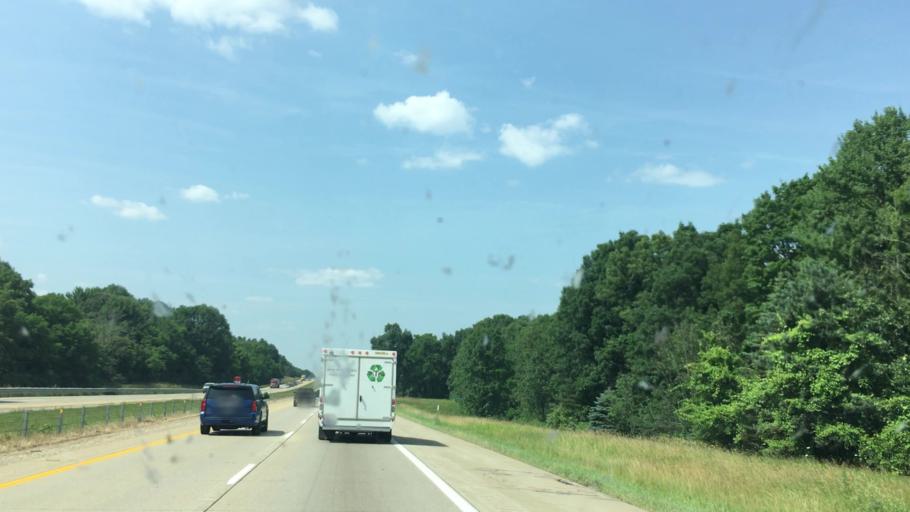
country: US
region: Michigan
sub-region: Allegan County
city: Plainwell
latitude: 42.4963
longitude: -85.6520
